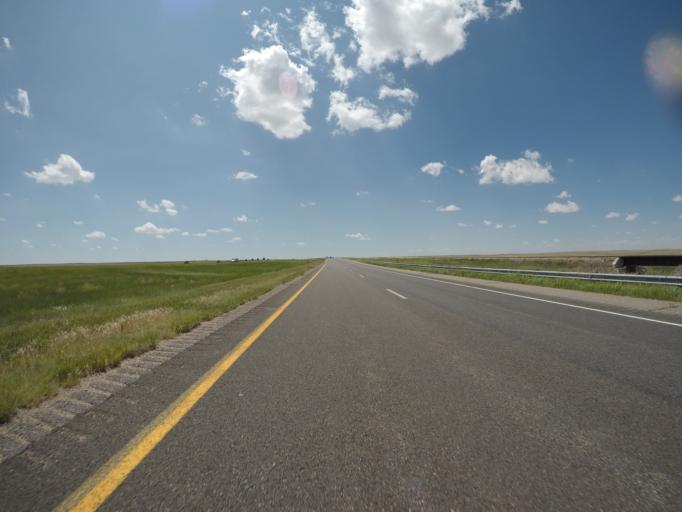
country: US
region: Colorado
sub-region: Lincoln County
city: Hugo
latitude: 39.2870
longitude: -103.1560
